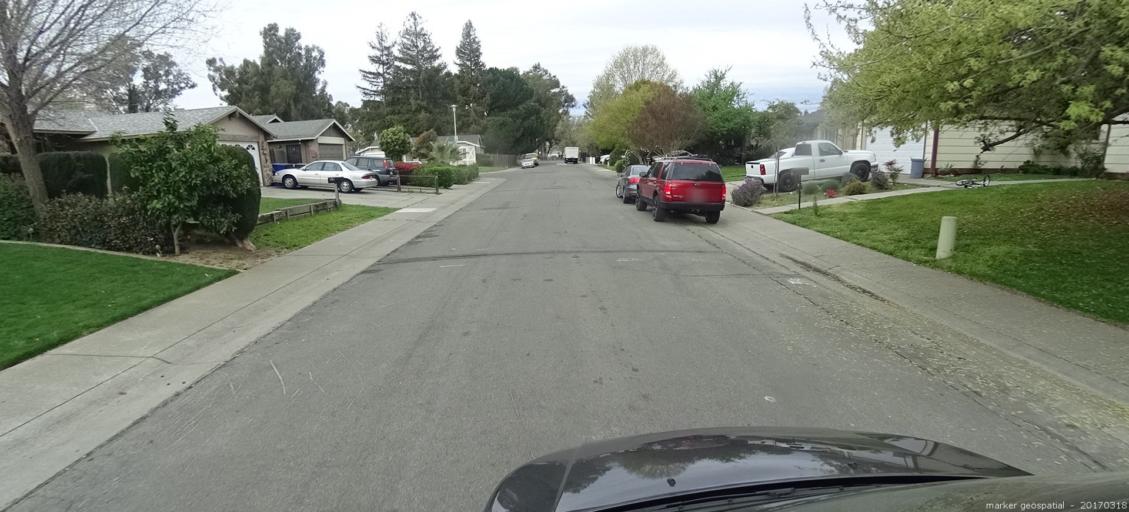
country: US
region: California
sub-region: Sacramento County
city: Parkway
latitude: 38.4859
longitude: -121.4626
